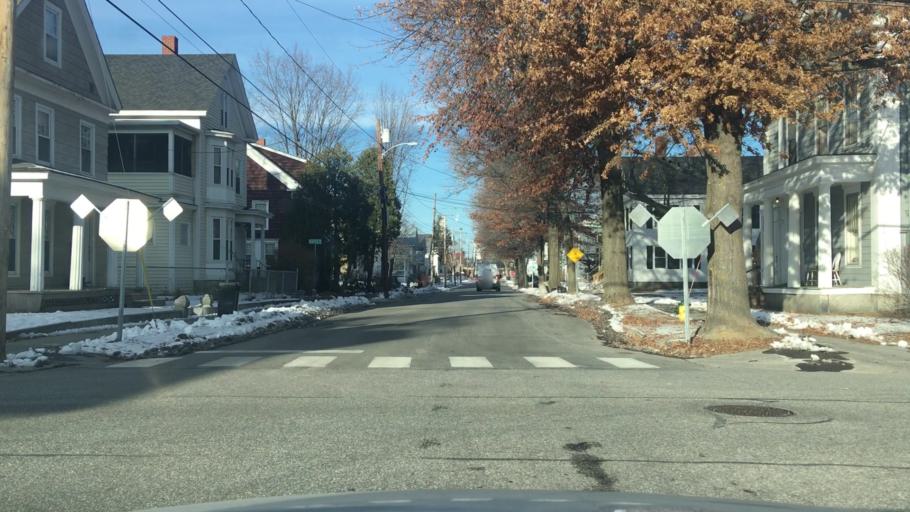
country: US
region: Maine
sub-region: Androscoggin County
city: Auburn
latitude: 44.0937
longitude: -70.2280
